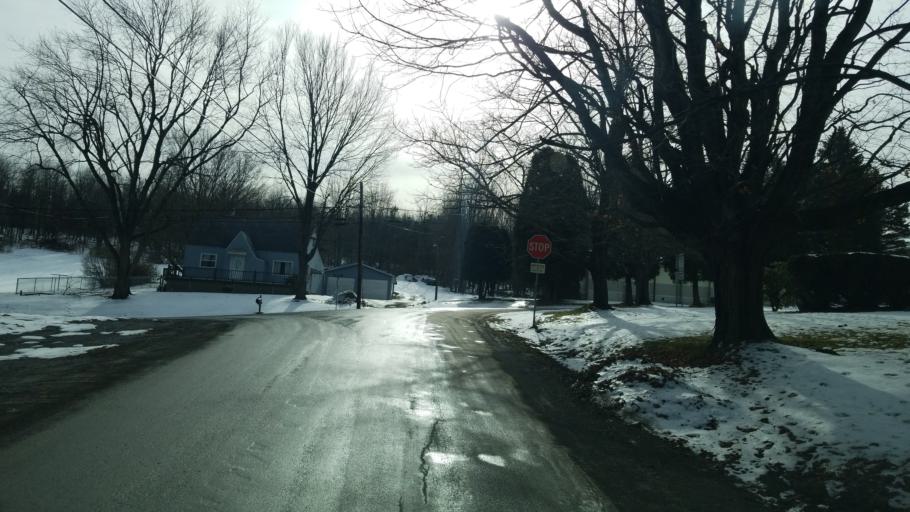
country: US
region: Pennsylvania
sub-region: Indiana County
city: Johnsonburg
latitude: 40.8369
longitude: -78.8728
